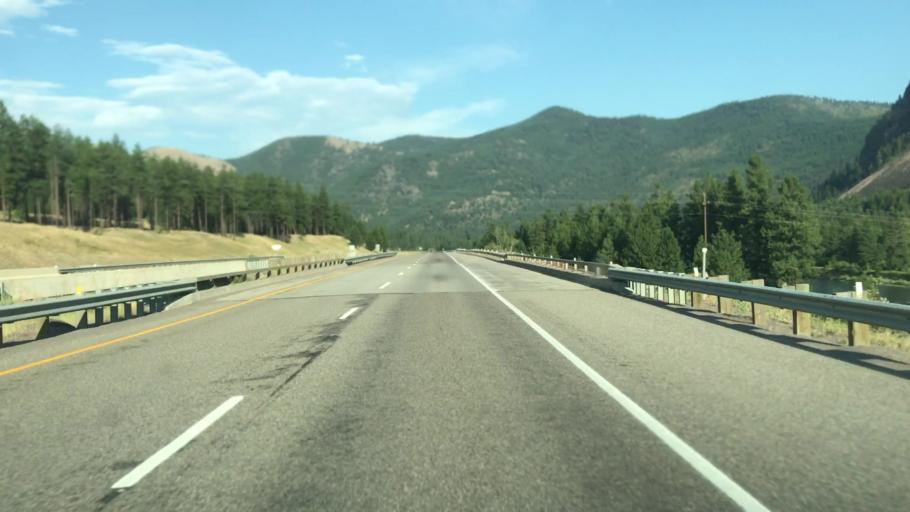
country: US
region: Montana
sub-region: Missoula County
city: Frenchtown
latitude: 46.9934
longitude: -114.4461
